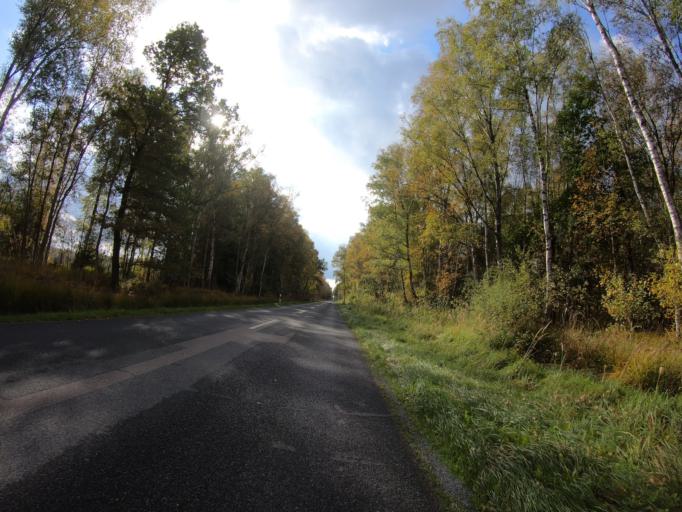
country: DE
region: Lower Saxony
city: Schoneworde
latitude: 52.5822
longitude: 10.6410
